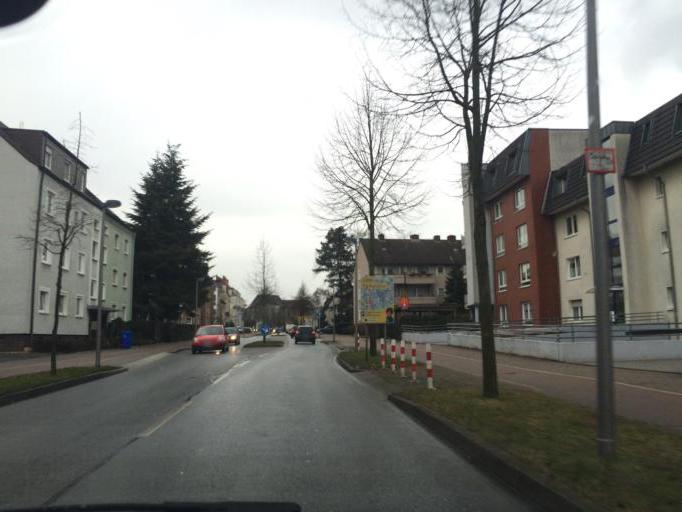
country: DE
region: North Rhine-Westphalia
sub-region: Regierungsbezirk Munster
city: Gladbeck
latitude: 51.5675
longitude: 6.9868
